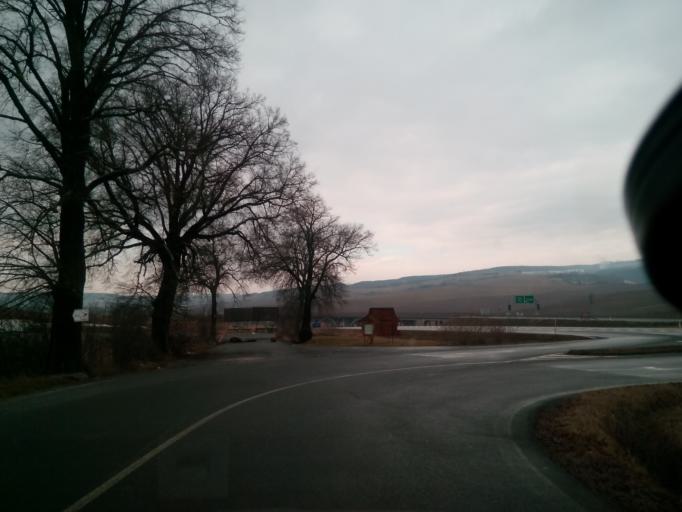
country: SK
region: Presovsky
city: Spisske Podhradie
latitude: 49.0077
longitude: 20.7250
